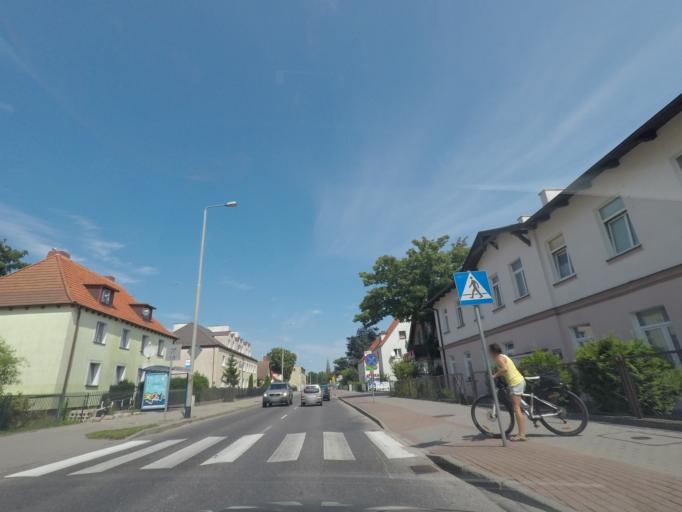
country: PL
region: Pomeranian Voivodeship
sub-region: Powiat slupski
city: Ustka
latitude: 54.5781
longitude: 16.8548
